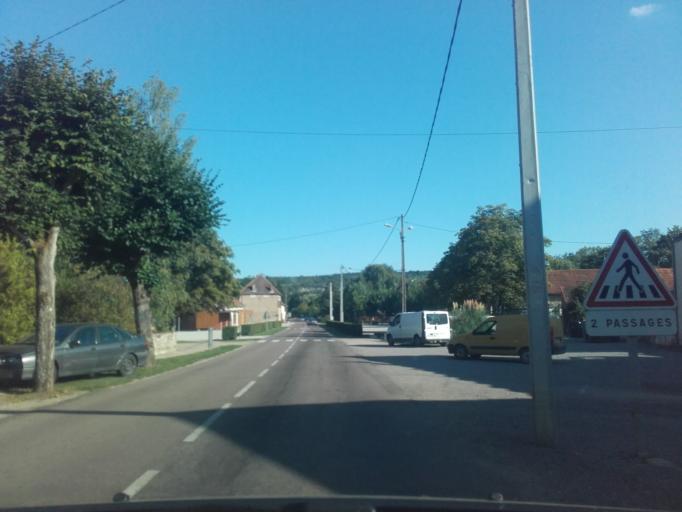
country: FR
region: Bourgogne
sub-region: Departement de Saone-et-Loire
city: Chagny
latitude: 46.9105
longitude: 4.7031
